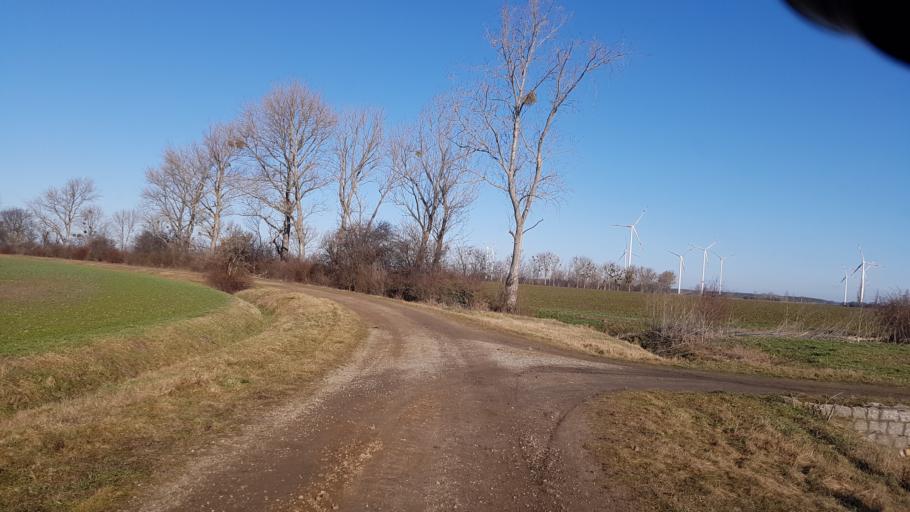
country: DE
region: Brandenburg
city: Muhlberg
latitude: 51.5014
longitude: 13.2230
